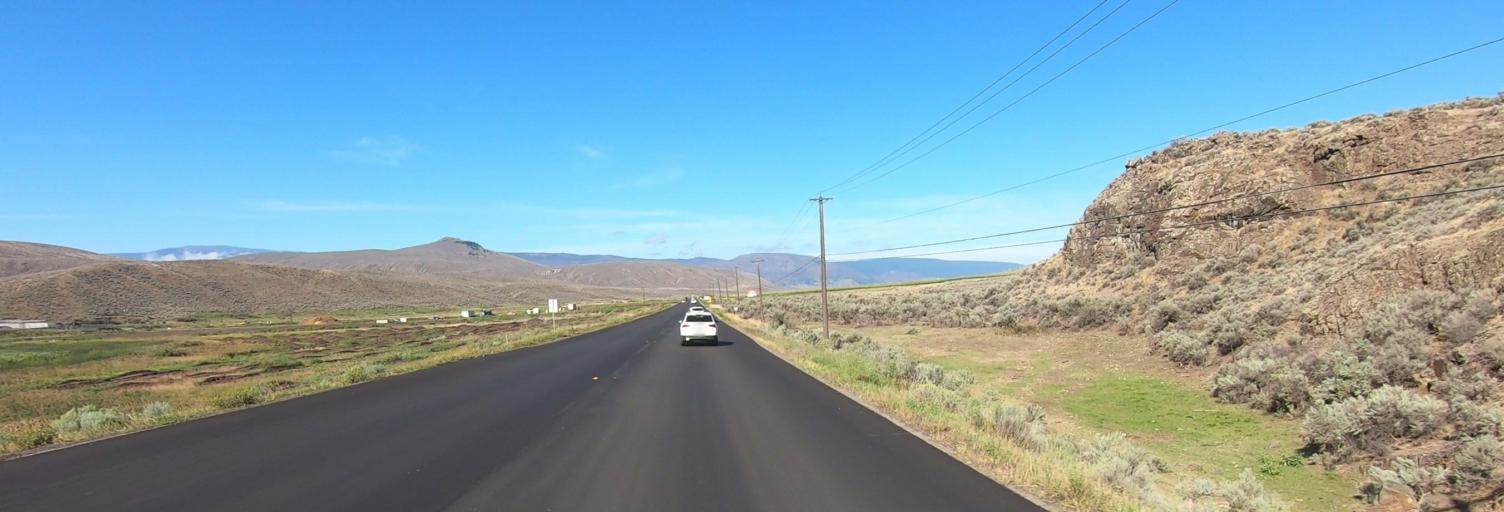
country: CA
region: British Columbia
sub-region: Thompson-Nicola Regional District
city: Ashcroft
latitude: 50.7861
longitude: -121.1893
